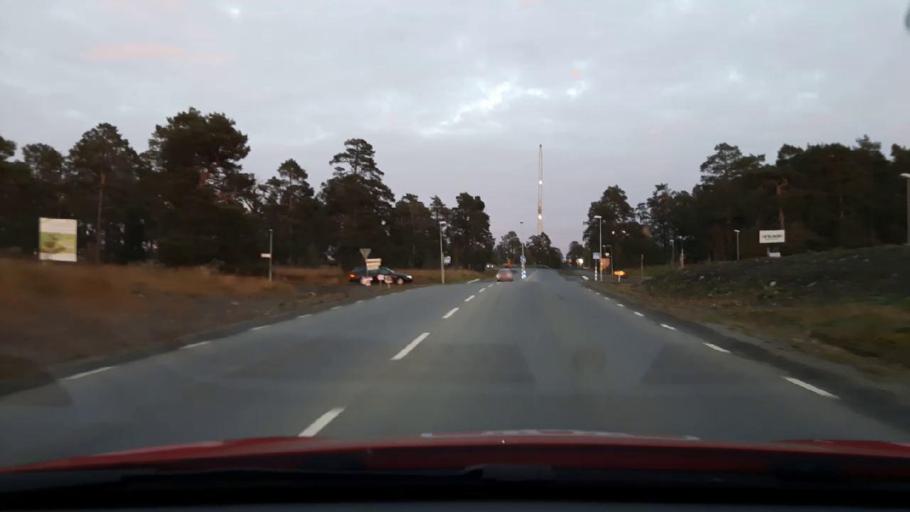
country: SE
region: Jaemtland
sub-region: OEstersunds Kommun
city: Ostersund
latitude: 63.1891
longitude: 14.6427
